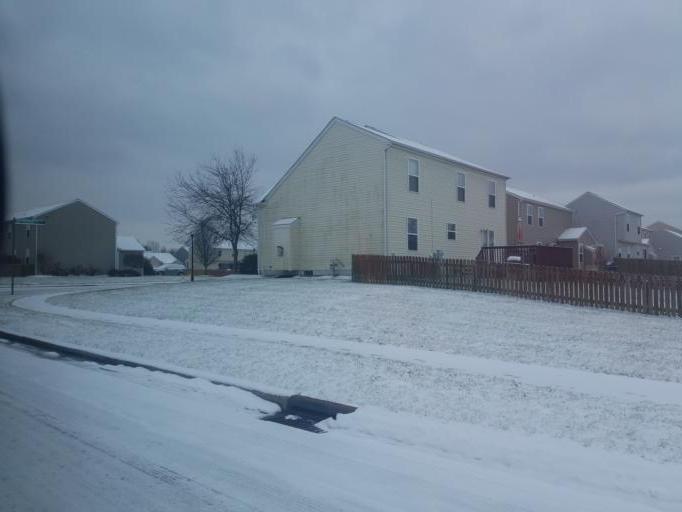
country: US
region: Ohio
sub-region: Franklin County
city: Reynoldsburg
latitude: 39.9982
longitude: -82.7982
